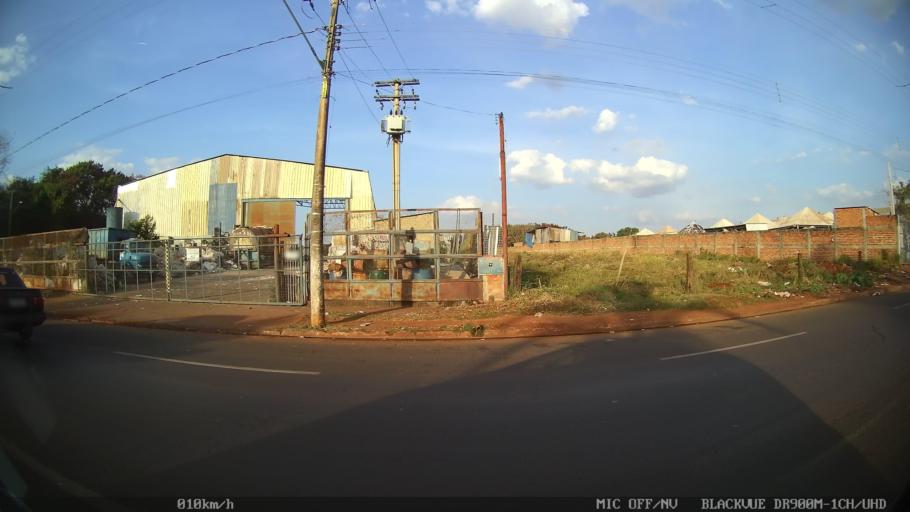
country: BR
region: Sao Paulo
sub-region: Ribeirao Preto
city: Ribeirao Preto
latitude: -21.1204
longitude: -47.8022
